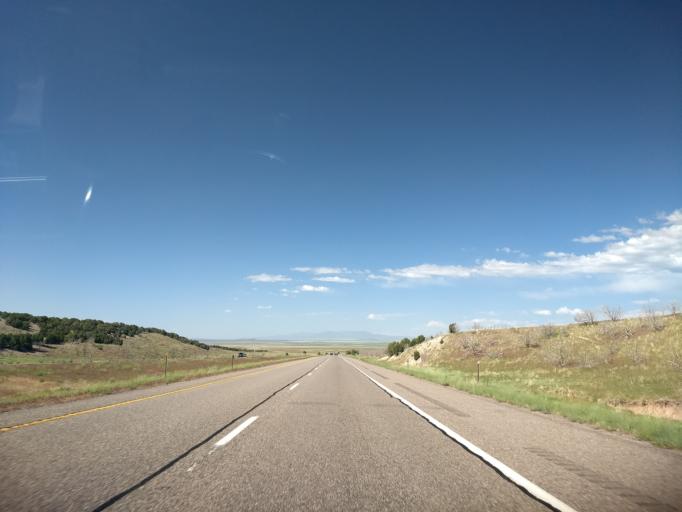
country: US
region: Utah
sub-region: Millard County
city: Fillmore
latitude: 38.7231
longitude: -112.5958
